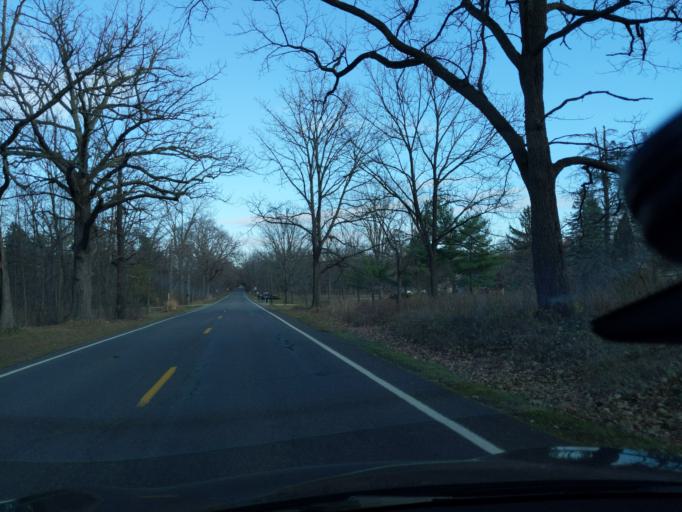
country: US
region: Michigan
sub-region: Ingham County
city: Haslett
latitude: 42.7153
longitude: -84.3520
